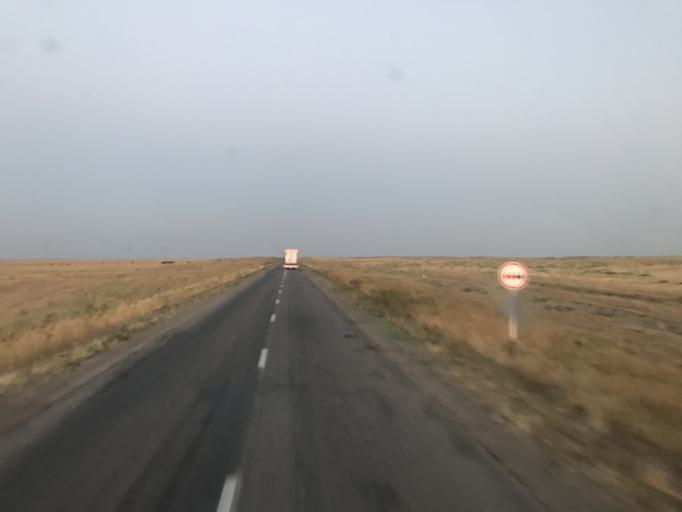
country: UZ
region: Toshkent
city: Chinoz
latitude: 41.1701
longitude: 68.6410
